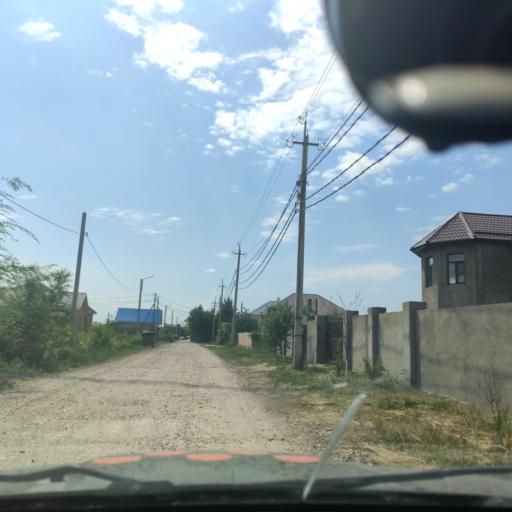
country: RU
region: Samara
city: Tol'yatti
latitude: 53.5766
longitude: 49.4086
